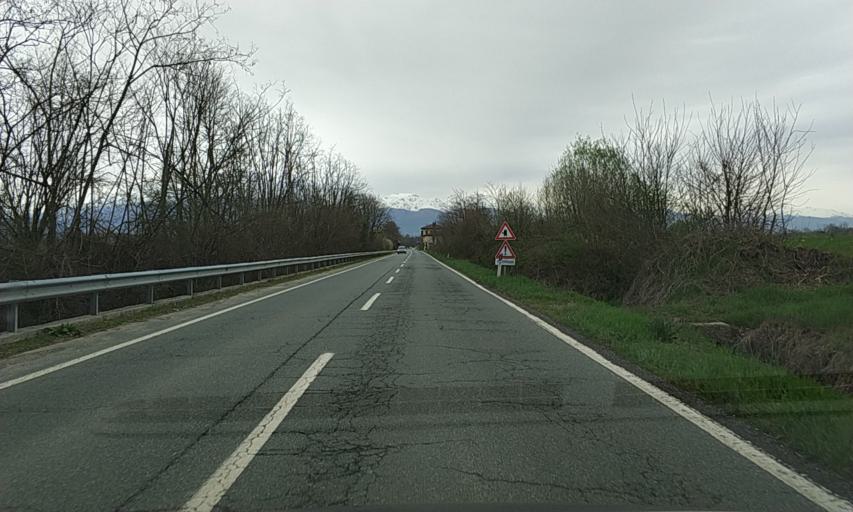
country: IT
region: Piedmont
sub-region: Provincia di Torino
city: Favria
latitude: 45.3055
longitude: 7.6776
